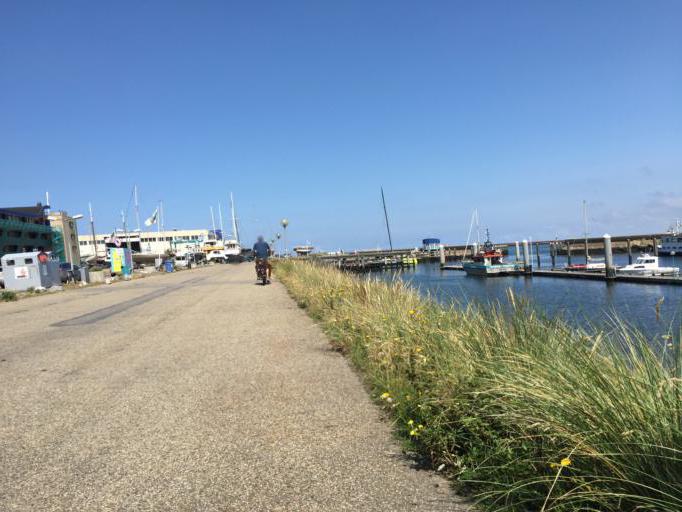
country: NL
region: North Holland
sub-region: Gemeente Bloemendaal
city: Bloemendaal
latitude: 52.4586
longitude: 4.5587
